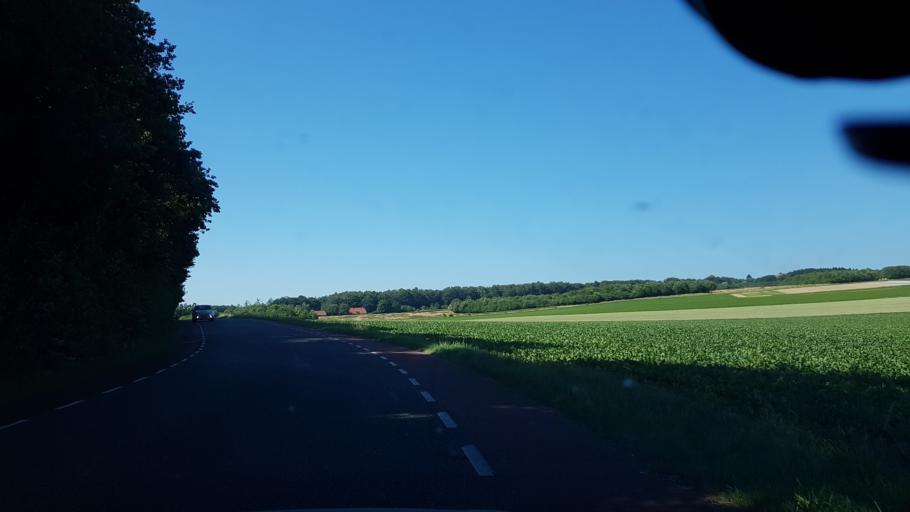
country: NL
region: Gelderland
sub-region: Gemeente Groesbeek
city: Bredeweg
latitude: 51.7473
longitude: 5.9530
